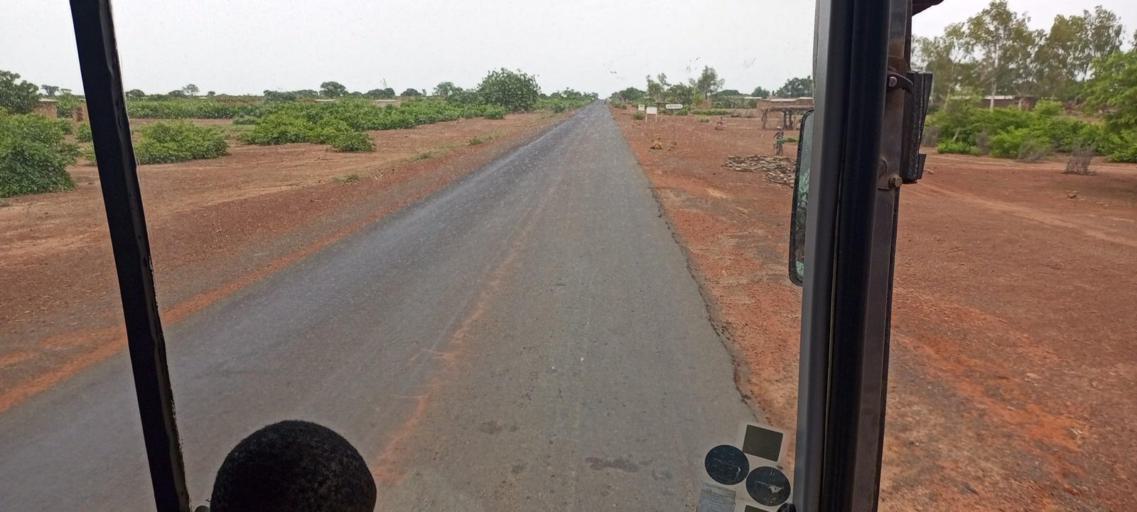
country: ML
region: Sikasso
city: Koutiala
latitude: 12.5398
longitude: -5.5746
